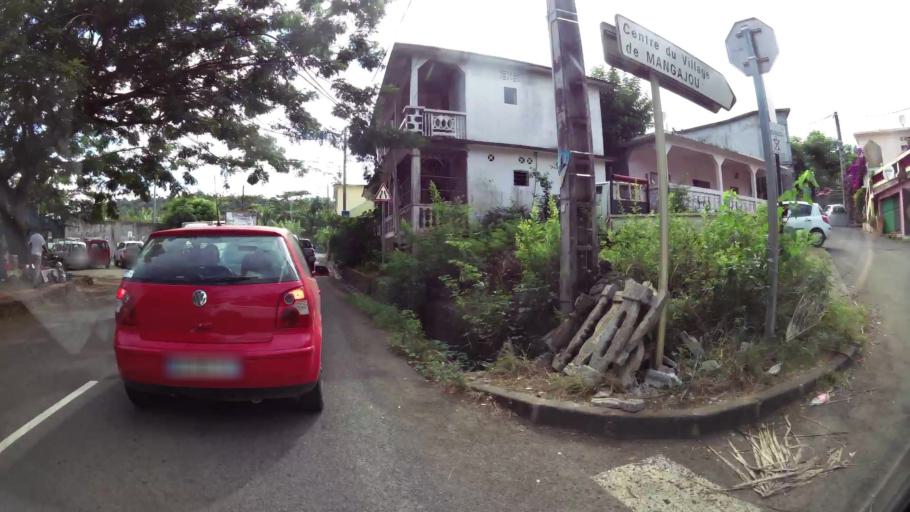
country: YT
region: Chiconi
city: Chiconi
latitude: -12.8446
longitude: 45.1160
